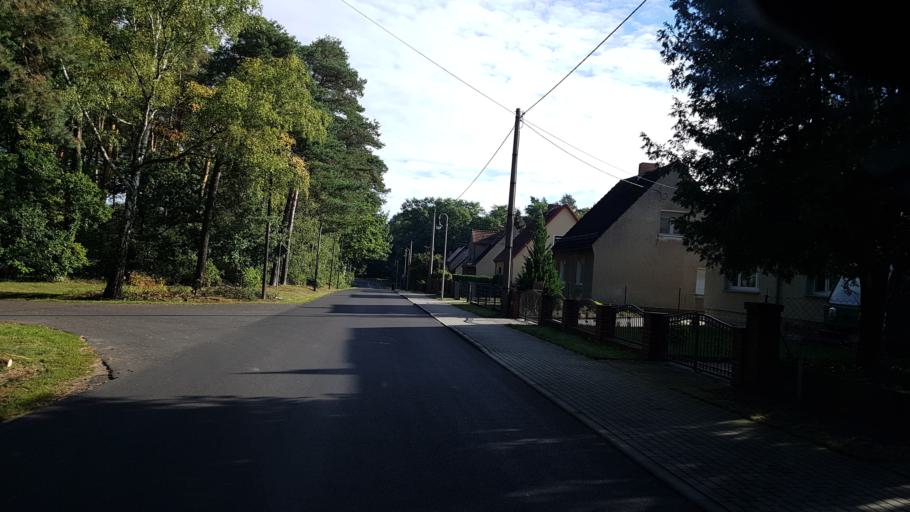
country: DE
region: Saxony
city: Gross Duben
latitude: 51.6278
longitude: 14.5441
